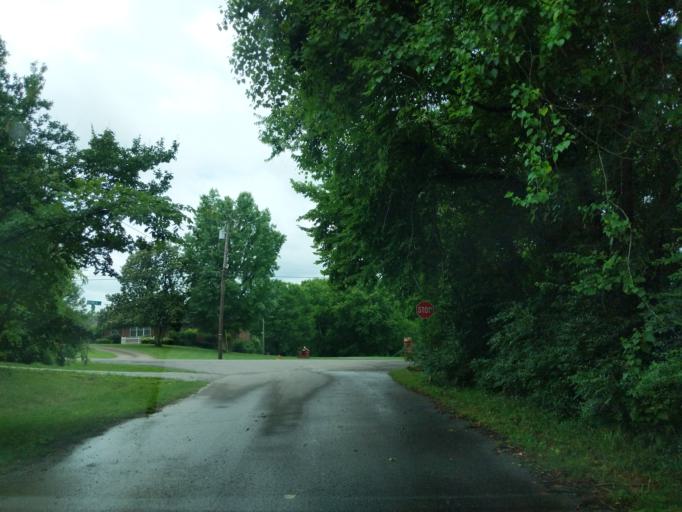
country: US
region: Tennessee
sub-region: Davidson County
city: Lakewood
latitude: 36.2391
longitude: -86.6783
